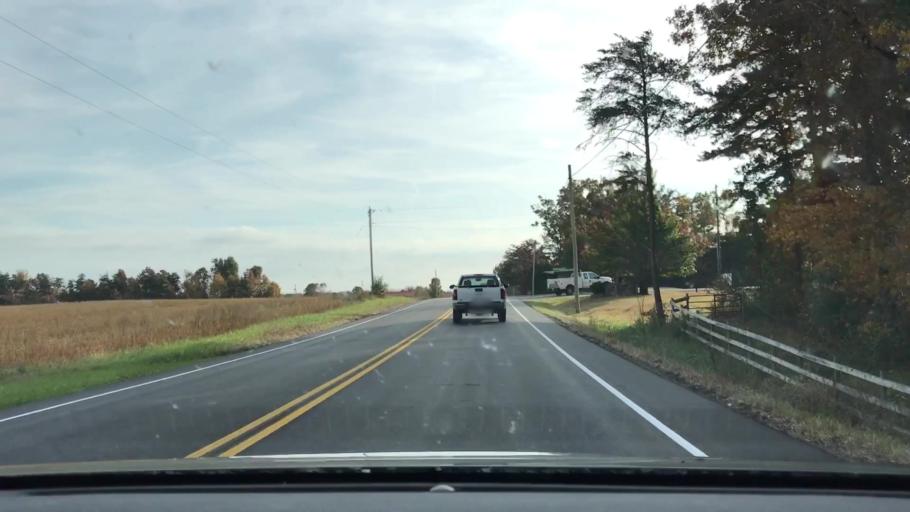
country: US
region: Tennessee
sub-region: Putnam County
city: Monterey
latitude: 36.1323
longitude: -85.1289
